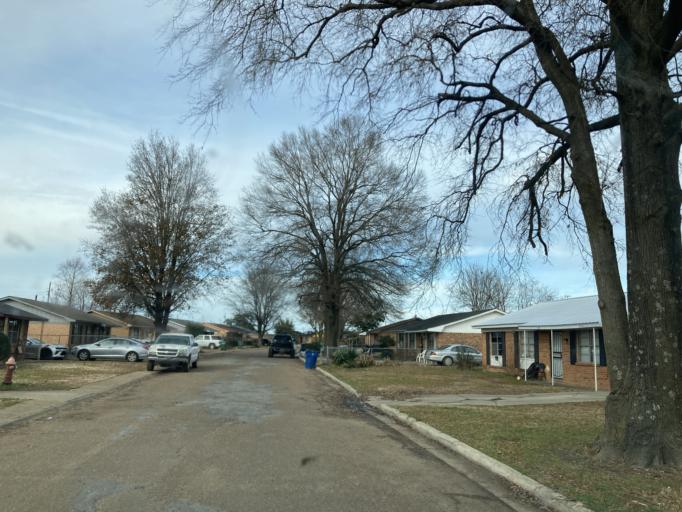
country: US
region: Mississippi
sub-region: Humphreys County
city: Belzoni
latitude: 33.1708
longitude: -90.5002
